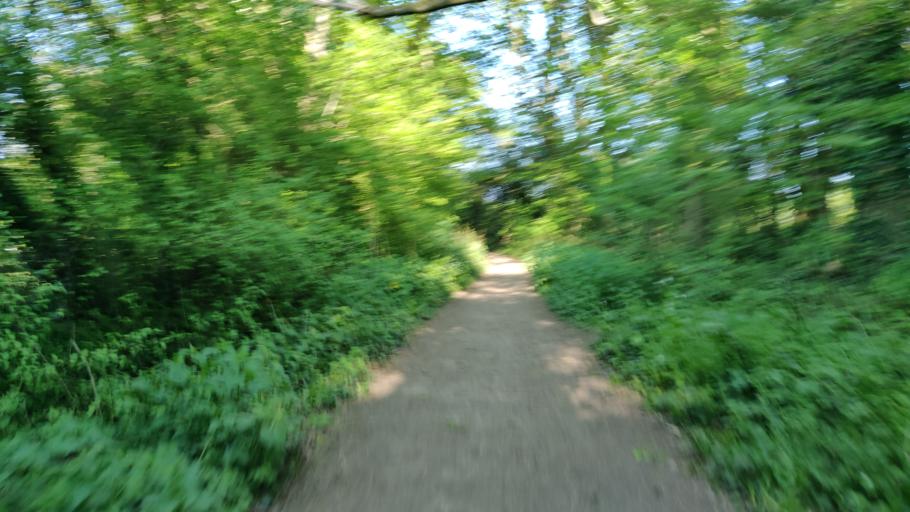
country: GB
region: England
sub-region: West Sussex
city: Southwater
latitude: 51.0600
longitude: -0.3712
